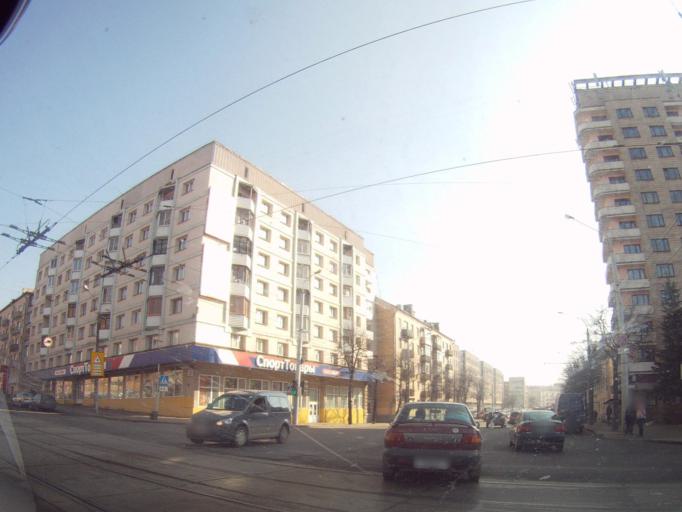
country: BY
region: Minsk
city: Minsk
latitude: 53.9262
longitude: 27.5940
